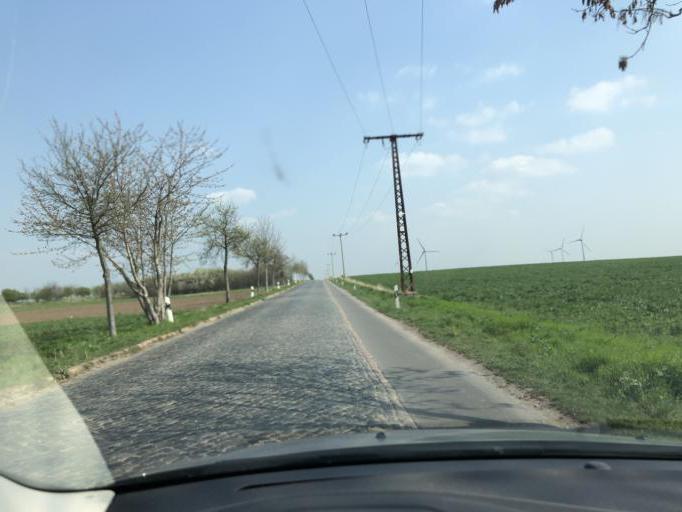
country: DE
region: Saxony-Anhalt
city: Landsberg
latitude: 51.5657
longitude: 12.1360
